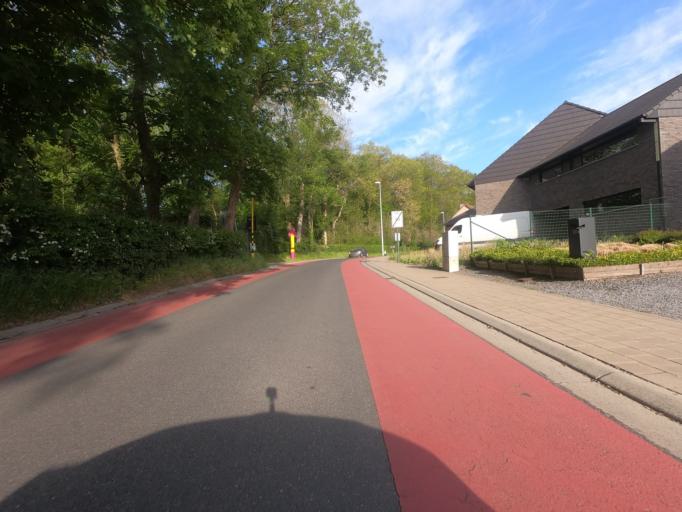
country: BE
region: Flanders
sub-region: Provincie Vlaams-Brabant
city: Galmaarden
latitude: 50.8022
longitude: 3.9687
